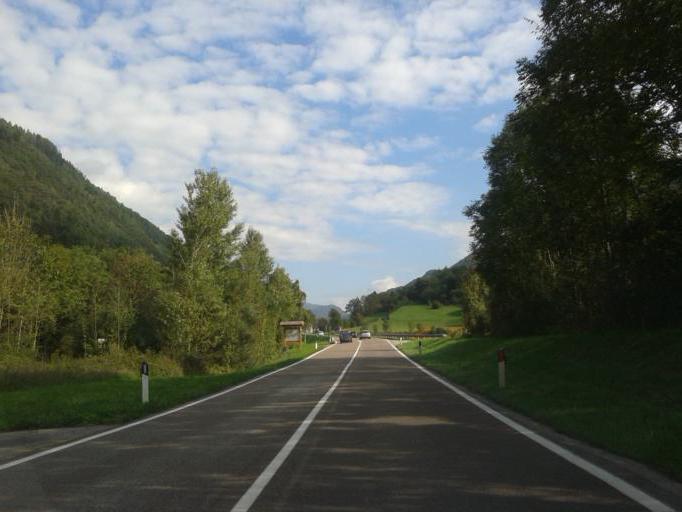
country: IT
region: Trentino-Alto Adige
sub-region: Provincia di Trento
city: Cimego
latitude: 45.9179
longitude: 10.6255
